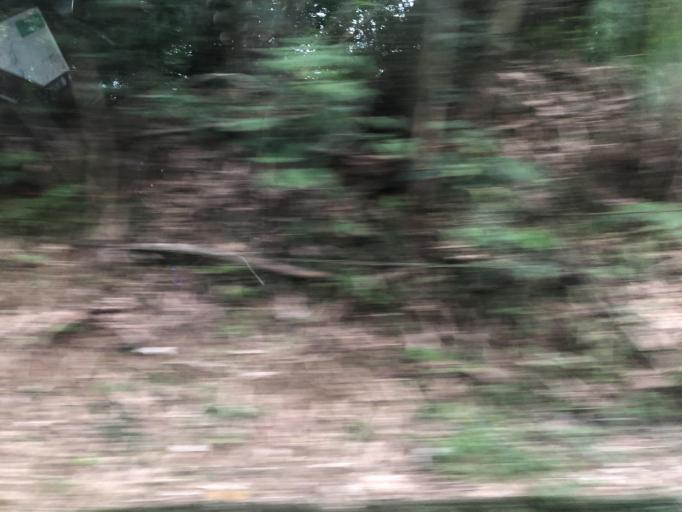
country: TW
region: Taiwan
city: Daxi
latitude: 24.9204
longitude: 121.3564
